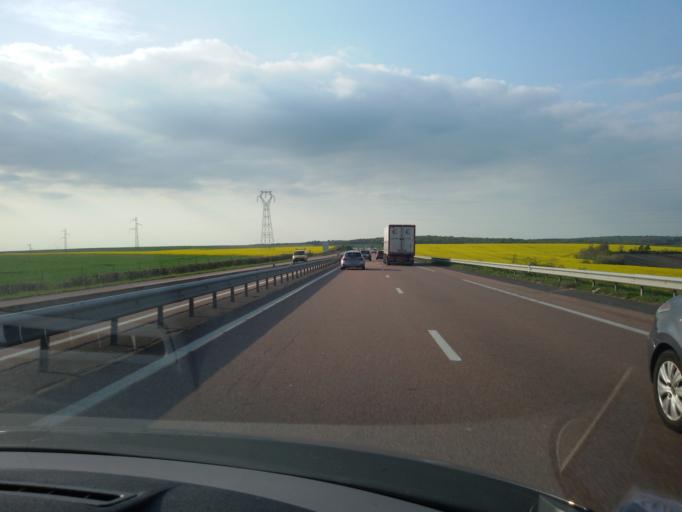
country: FR
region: Champagne-Ardenne
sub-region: Departement de l'Aube
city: Bar-sur-Aube
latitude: 48.1495
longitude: 4.6085
